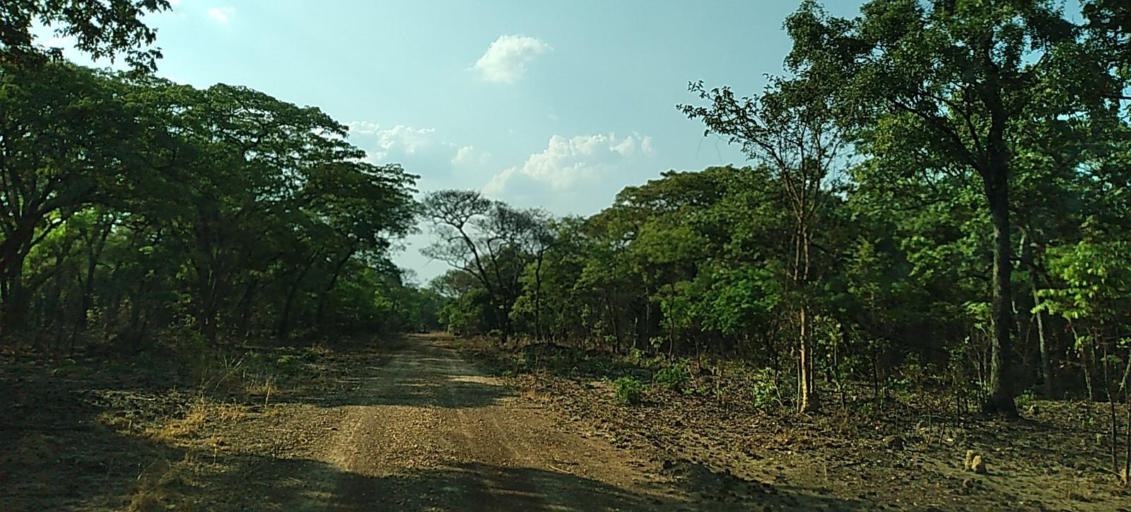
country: ZM
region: Copperbelt
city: Mpongwe
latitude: -13.3880
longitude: 28.0096
